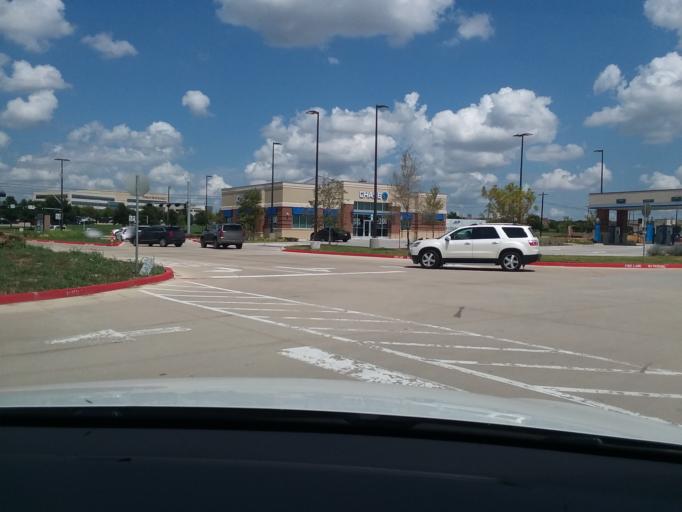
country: US
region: Texas
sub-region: Collin County
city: McKinney
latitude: 33.2173
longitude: -96.6826
